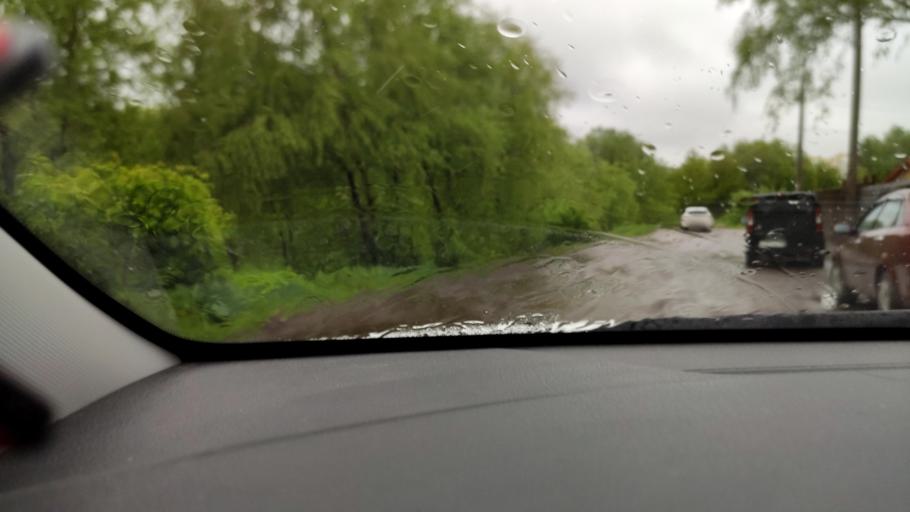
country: RU
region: Tatarstan
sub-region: Gorod Kazan'
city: Kazan
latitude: 55.8095
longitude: 49.2127
